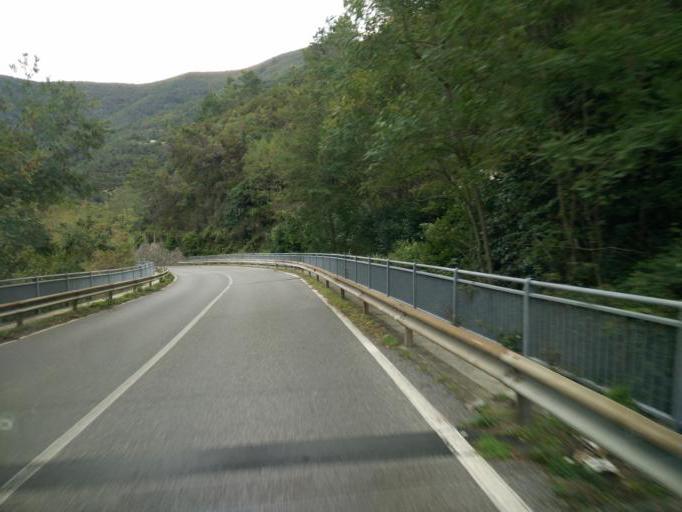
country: IT
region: Liguria
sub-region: Provincia di La Spezia
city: Riomaggiore
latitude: 44.0987
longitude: 9.7480
